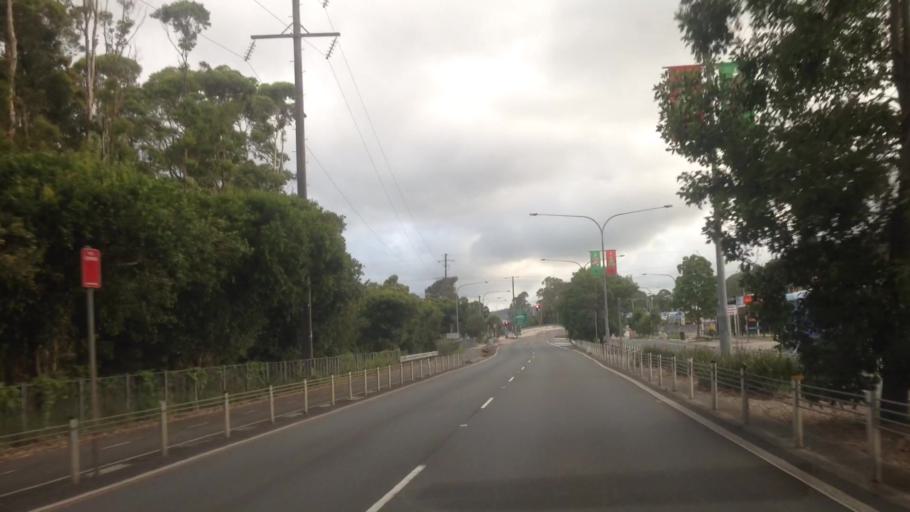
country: AU
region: New South Wales
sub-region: Wyong Shire
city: Chittaway Bay
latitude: -33.3053
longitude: 151.4203
